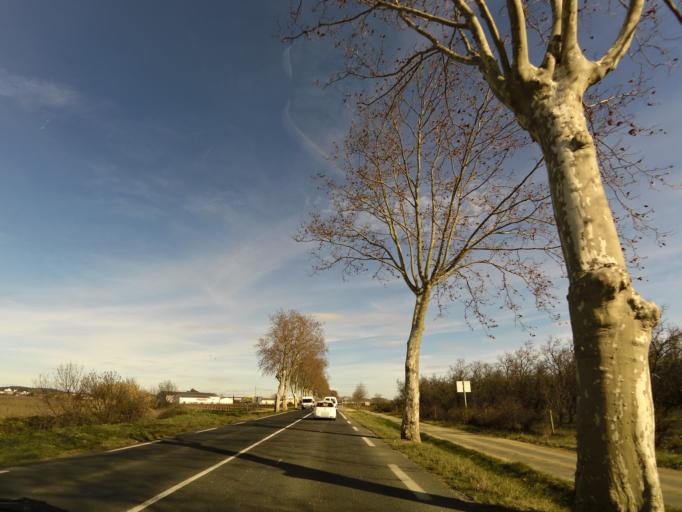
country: FR
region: Languedoc-Roussillon
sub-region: Departement du Gard
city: Aimargues
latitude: 43.7102
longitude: 4.1962
